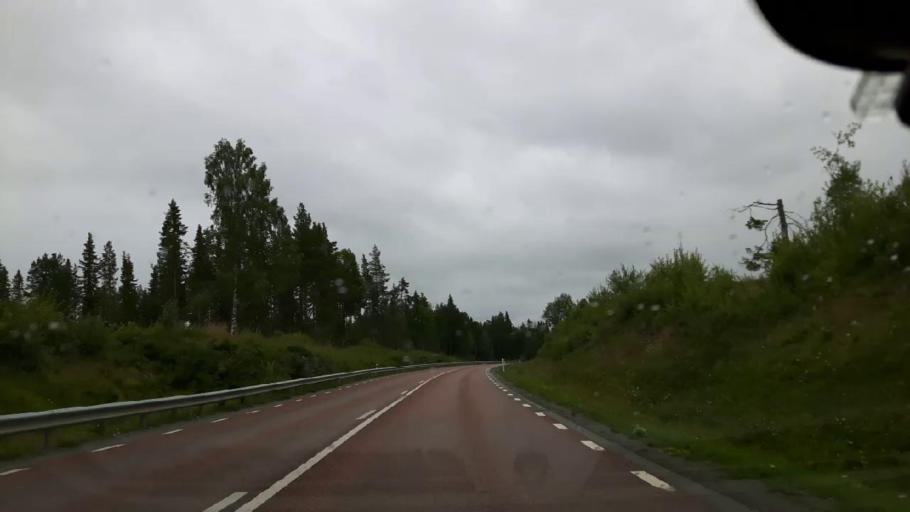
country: SE
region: Jaemtland
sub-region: Bergs Kommun
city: Hoverberg
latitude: 62.9496
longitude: 14.5446
